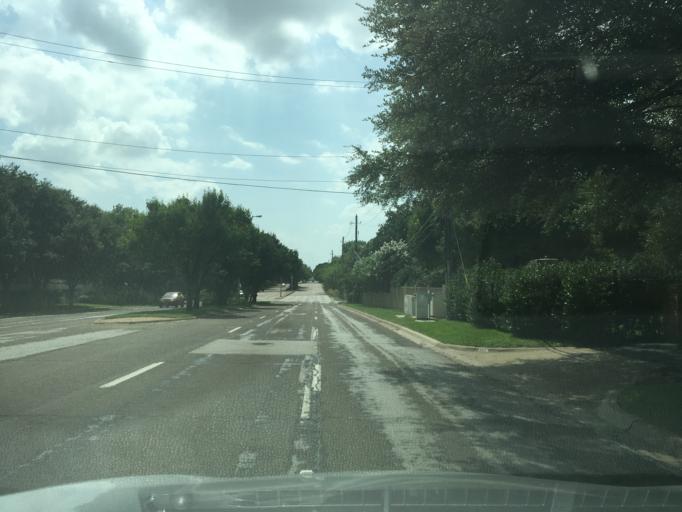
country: US
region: Texas
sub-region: Dallas County
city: University Park
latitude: 32.8950
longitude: -96.8200
